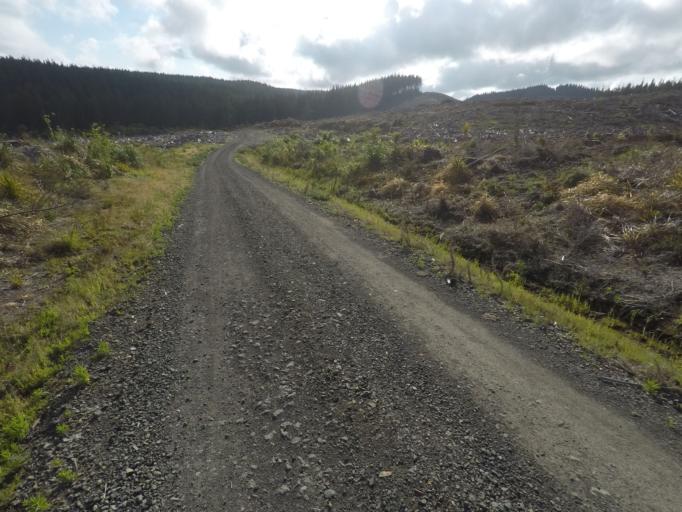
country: NZ
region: Auckland
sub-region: Auckland
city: Parakai
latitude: -36.7130
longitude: 174.5696
